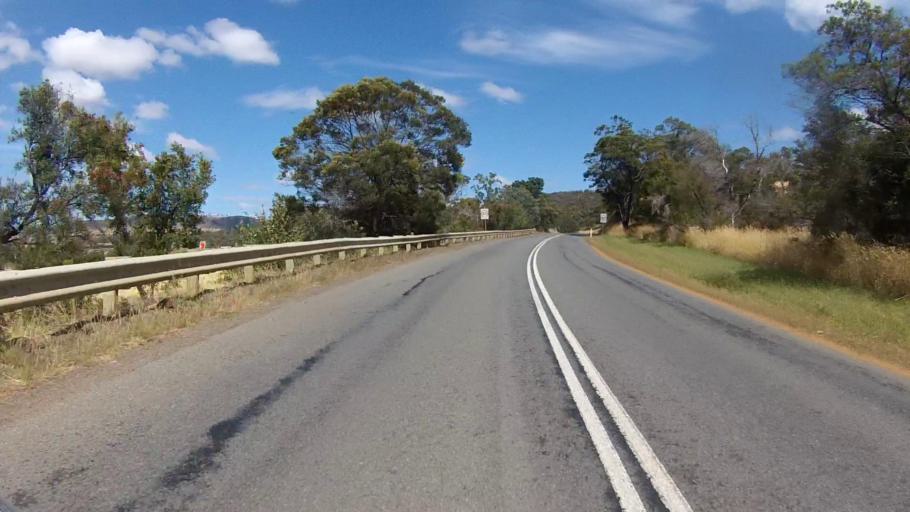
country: AU
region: Tasmania
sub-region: Clarence
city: Cambridge
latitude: -42.6568
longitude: 147.4302
